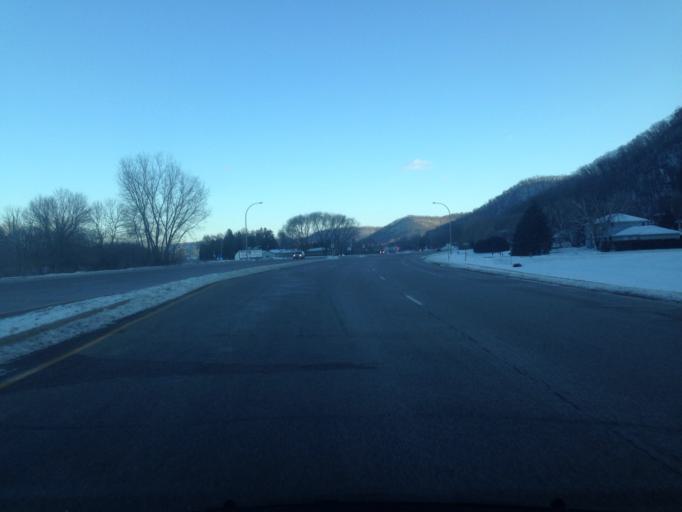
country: US
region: Minnesota
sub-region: Winona County
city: Goodview
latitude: 44.0815
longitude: -91.7355
